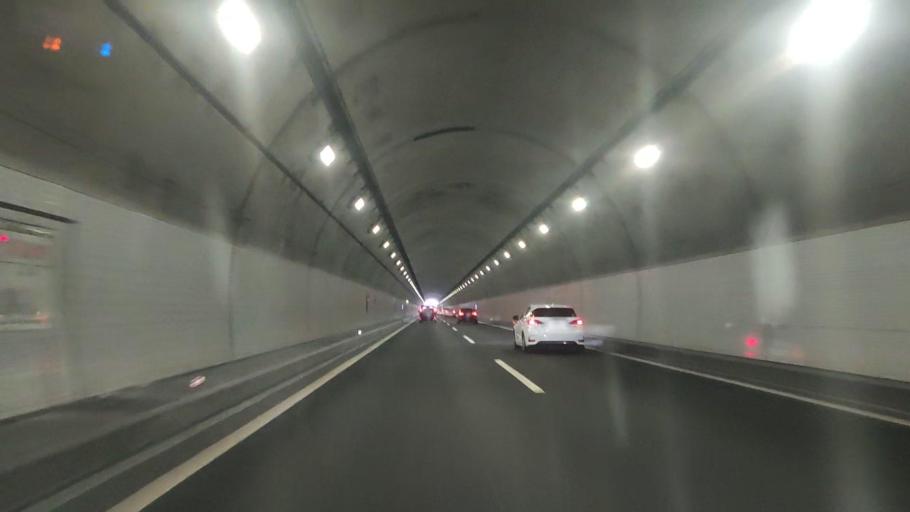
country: JP
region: Fukuoka
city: Kanda
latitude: 33.8104
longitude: 130.9121
